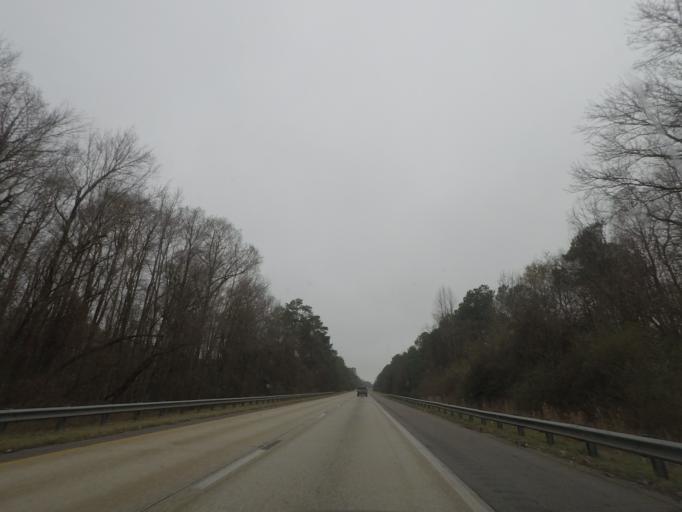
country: US
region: South Carolina
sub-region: Clarendon County
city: Manning
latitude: 33.7254
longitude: -80.2247
